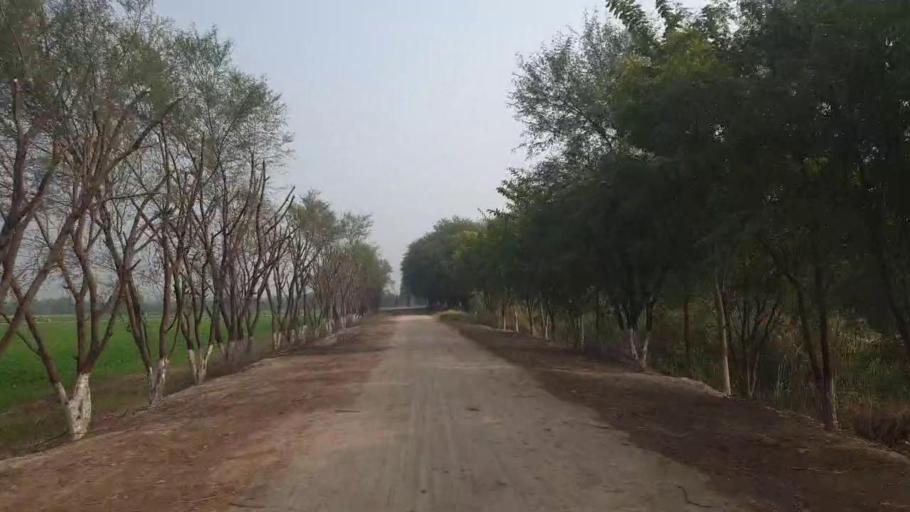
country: PK
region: Sindh
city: Tando Adam
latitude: 25.7766
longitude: 68.5836
